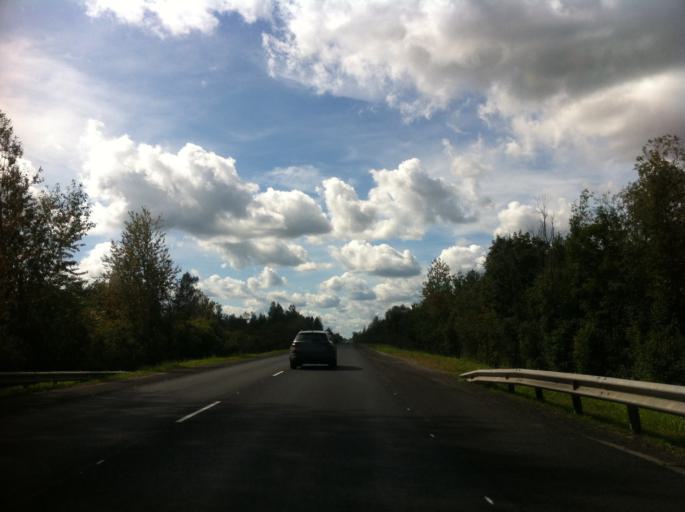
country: RU
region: Pskov
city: Izborsk
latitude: 57.7528
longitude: 28.0586
